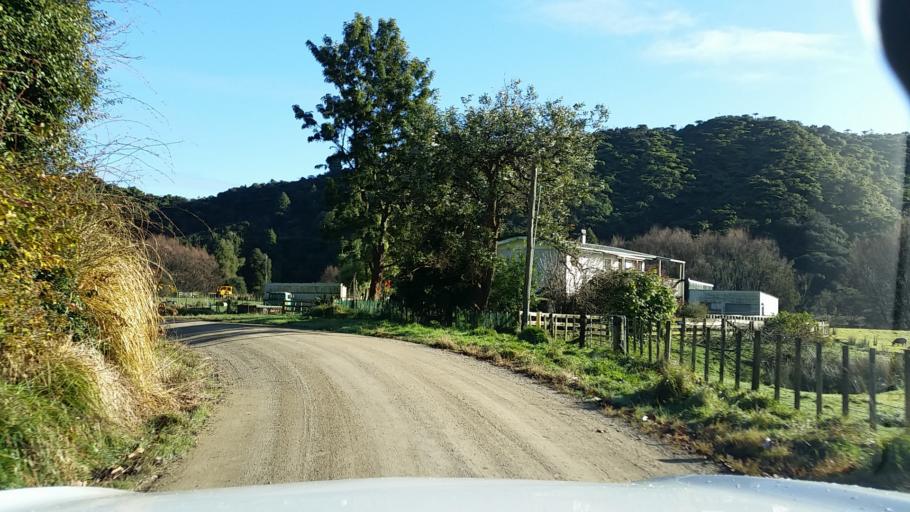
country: NZ
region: Taranaki
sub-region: South Taranaki District
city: Patea
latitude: -39.6995
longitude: 174.7350
